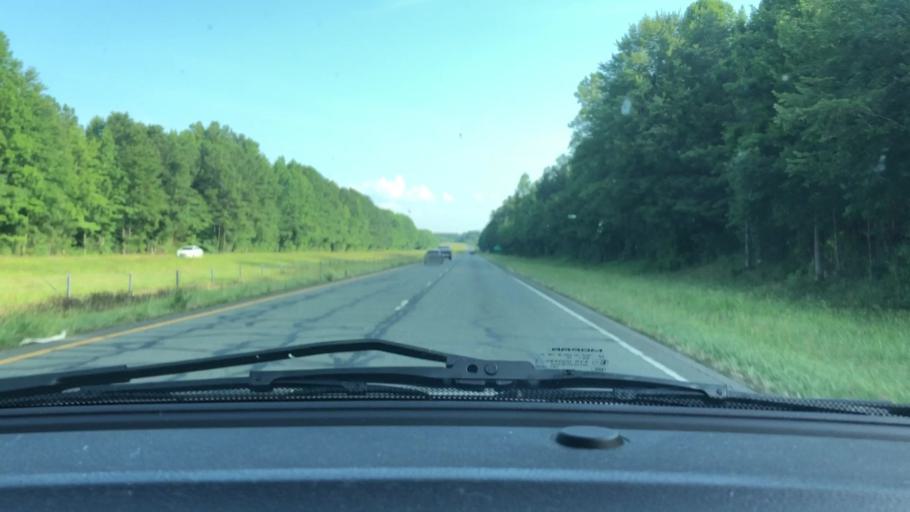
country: US
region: North Carolina
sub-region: Chatham County
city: Siler City
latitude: 35.7097
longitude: -79.4293
